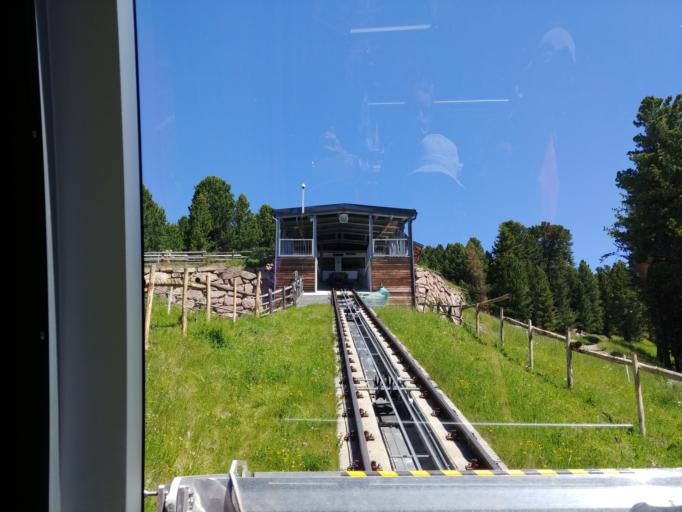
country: IT
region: Trentino-Alto Adige
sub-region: Bolzano
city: Ortisei
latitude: 46.5990
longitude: 11.6780
